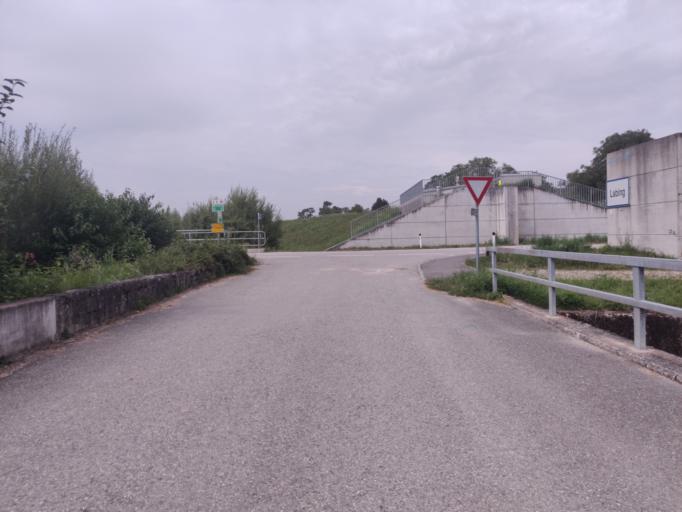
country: AT
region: Lower Austria
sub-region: Politischer Bezirk Amstetten
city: Strengberg
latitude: 48.1888
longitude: 14.7181
